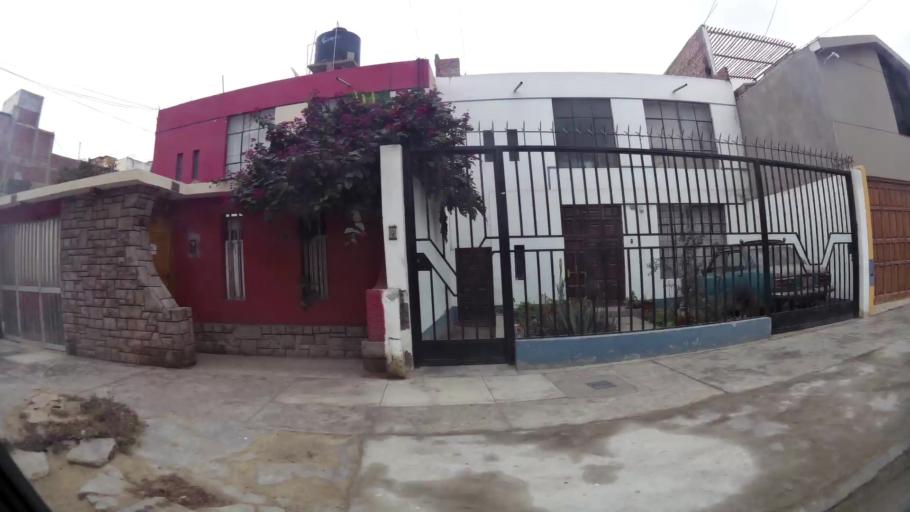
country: PE
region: La Libertad
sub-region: Provincia de Trujillo
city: Trujillo
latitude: -8.1210
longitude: -79.0390
